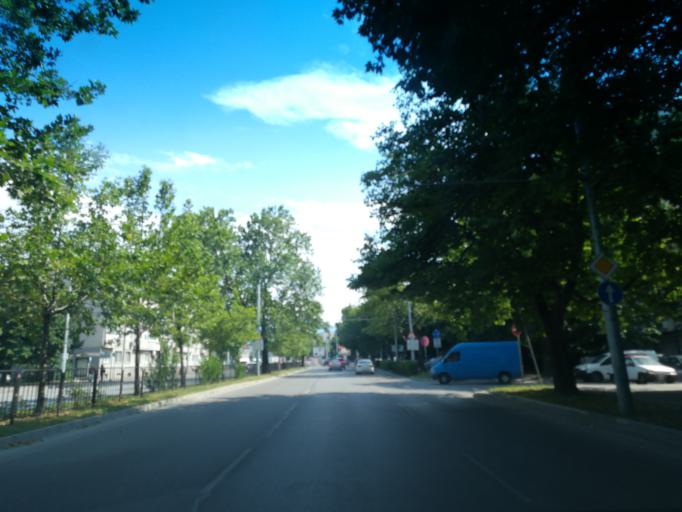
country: BG
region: Plovdiv
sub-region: Obshtina Plovdiv
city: Plovdiv
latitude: 42.1377
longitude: 24.7629
